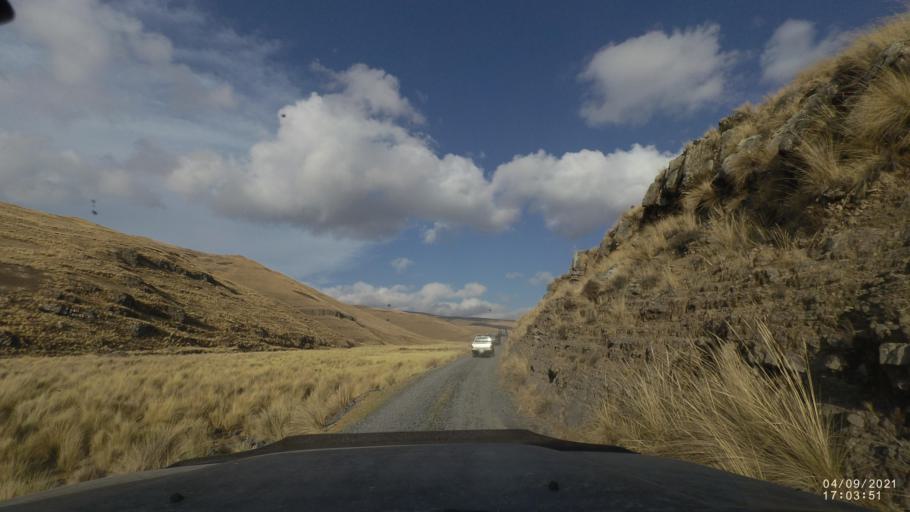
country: BO
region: Cochabamba
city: Cochabamba
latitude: -17.1756
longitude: -66.2794
